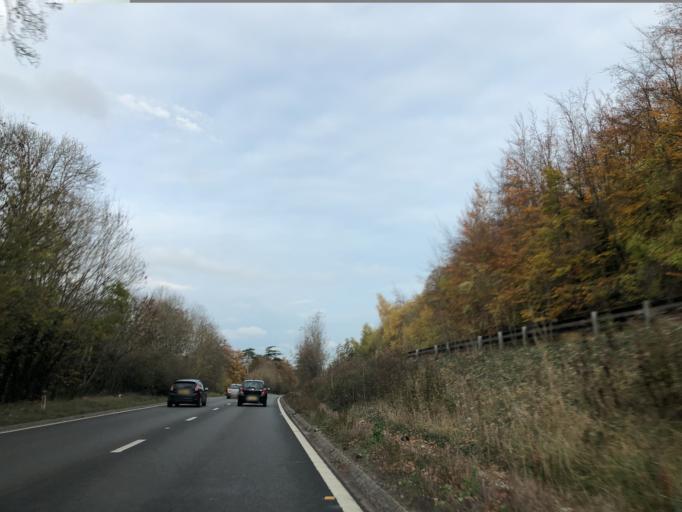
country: GB
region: England
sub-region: Royal Borough of Windsor and Maidenhead
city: Bisham
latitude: 51.5453
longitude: -0.7852
